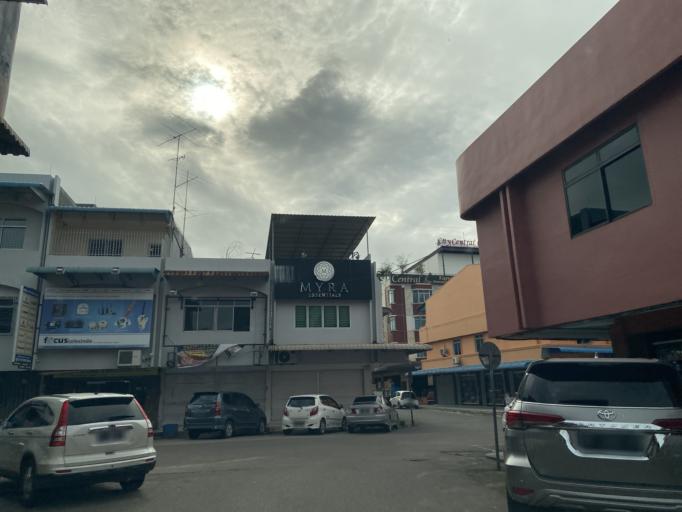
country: SG
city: Singapore
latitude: 1.1463
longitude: 104.0093
